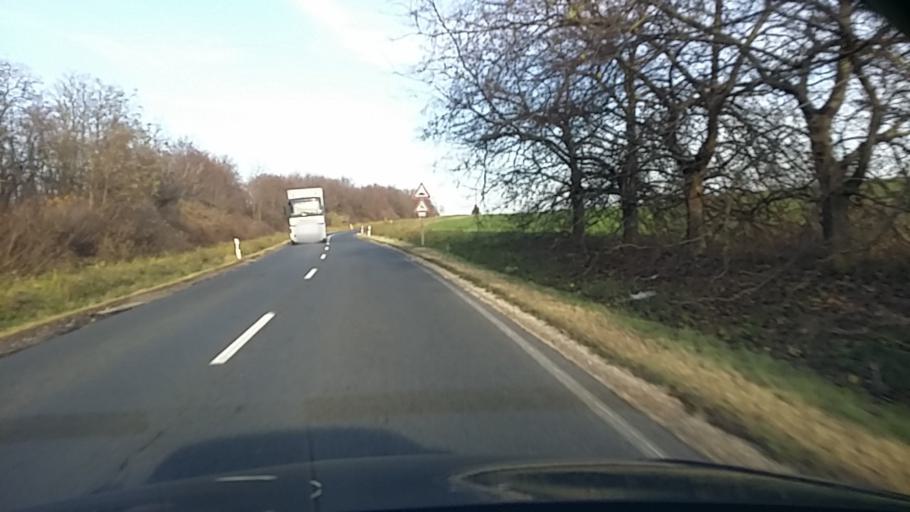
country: HU
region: Veszprem
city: Nemesvamos
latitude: 47.0295
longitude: 17.8087
